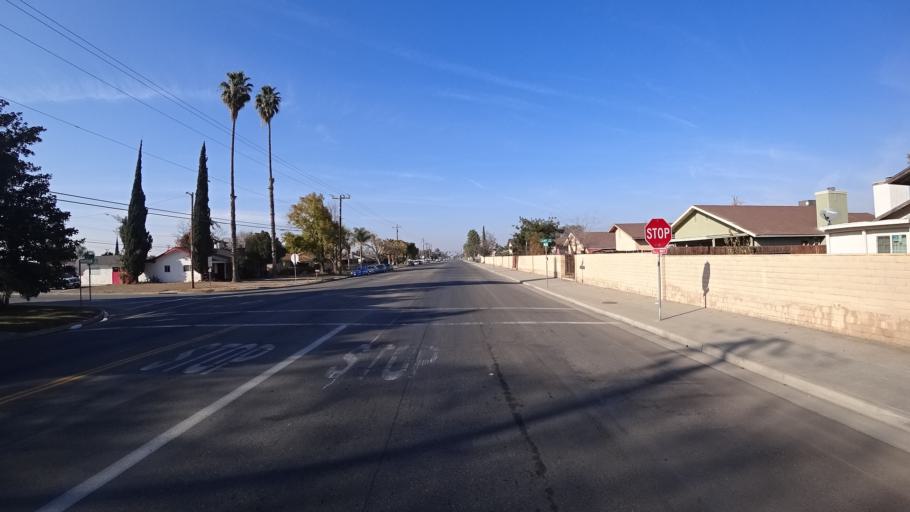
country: US
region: California
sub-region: Kern County
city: Greenfield
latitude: 35.3032
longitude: -119.0183
